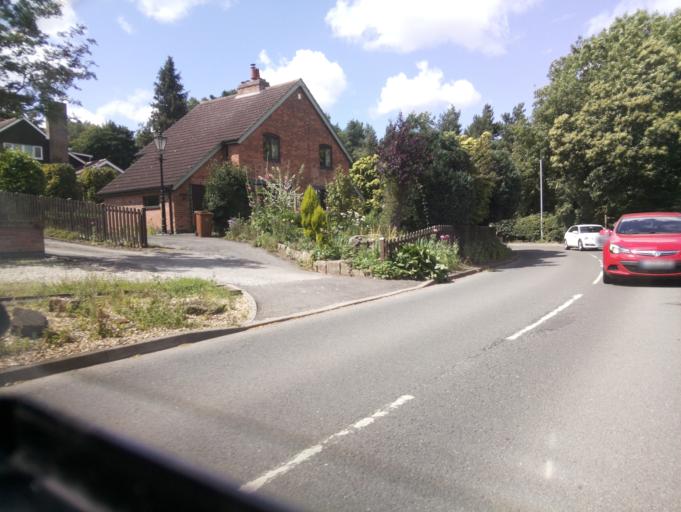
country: GB
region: England
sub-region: Nottinghamshire
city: Lowdham
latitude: 53.0127
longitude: -1.0104
